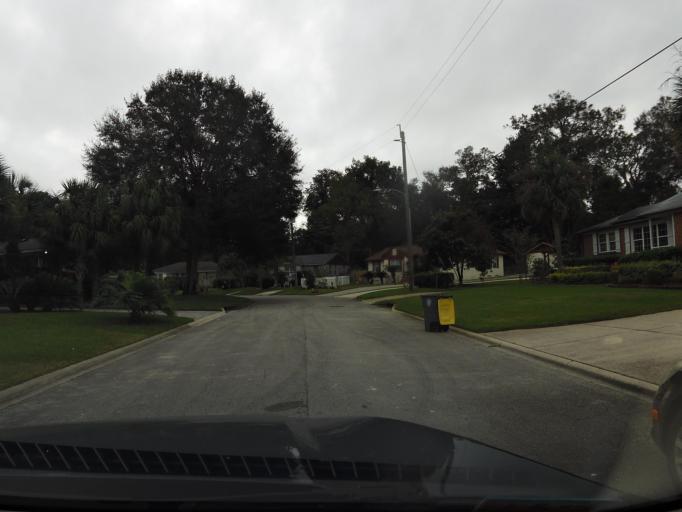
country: US
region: Florida
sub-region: Duval County
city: Jacksonville
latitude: 30.3100
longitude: -81.6019
